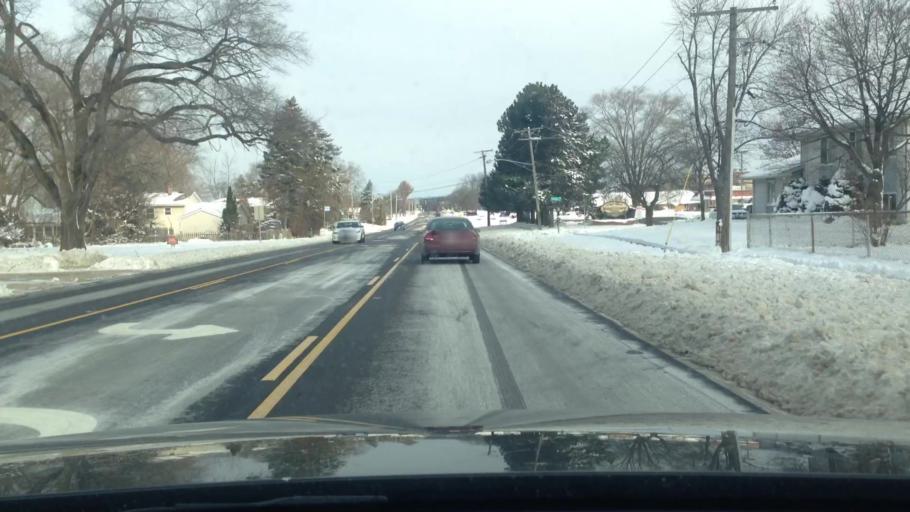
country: US
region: Illinois
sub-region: McHenry County
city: Woodstock
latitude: 42.3358
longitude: -88.4432
